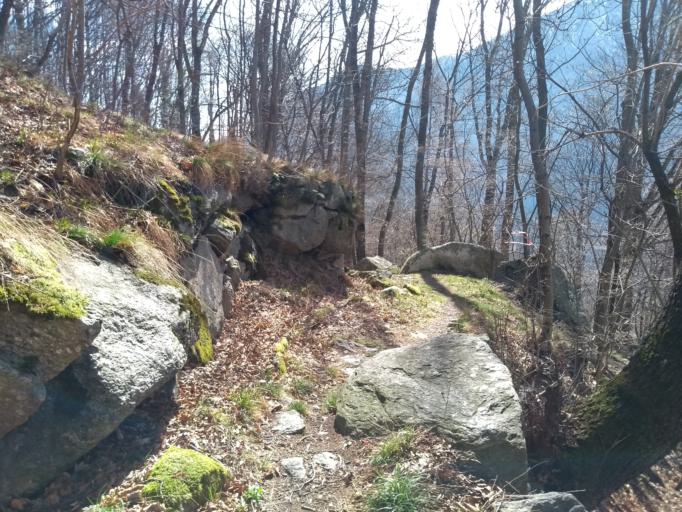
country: IT
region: Piedmont
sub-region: Provincia di Torino
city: Chialamberto
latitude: 45.3699
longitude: 7.3472
